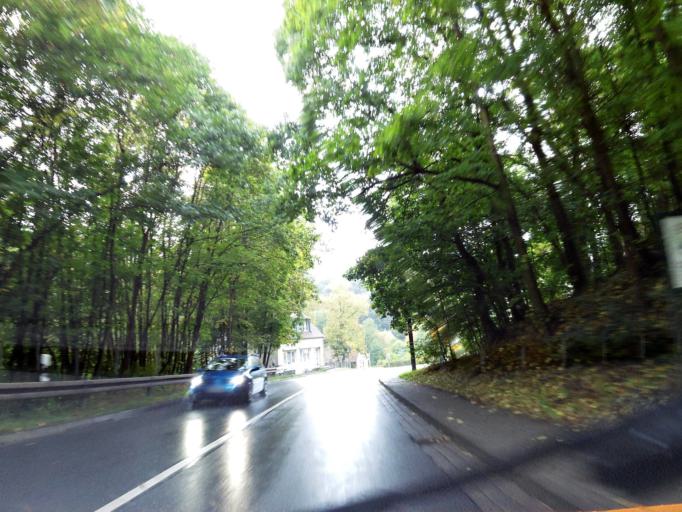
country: DE
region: Saxony-Anhalt
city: Harzgerode
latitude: 51.6701
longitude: 11.1333
